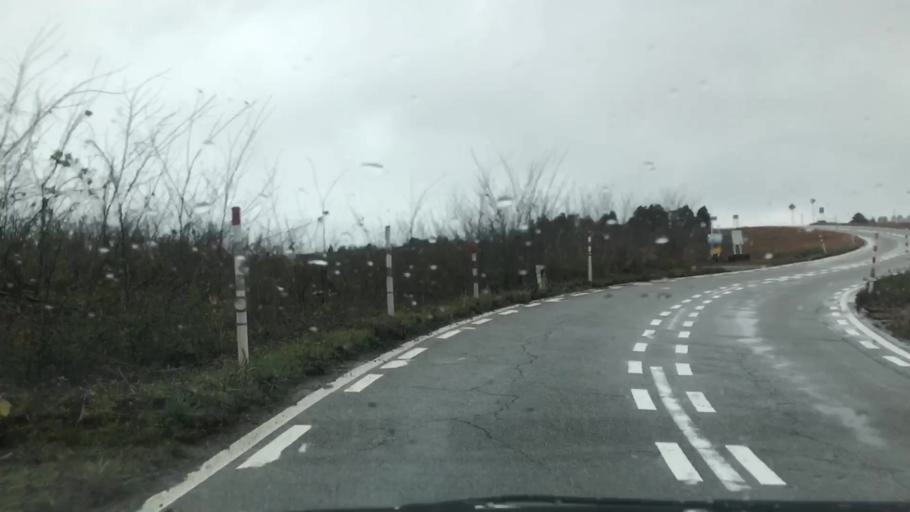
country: JP
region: Toyama
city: Kamiichi
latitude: 36.6272
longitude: 137.3000
